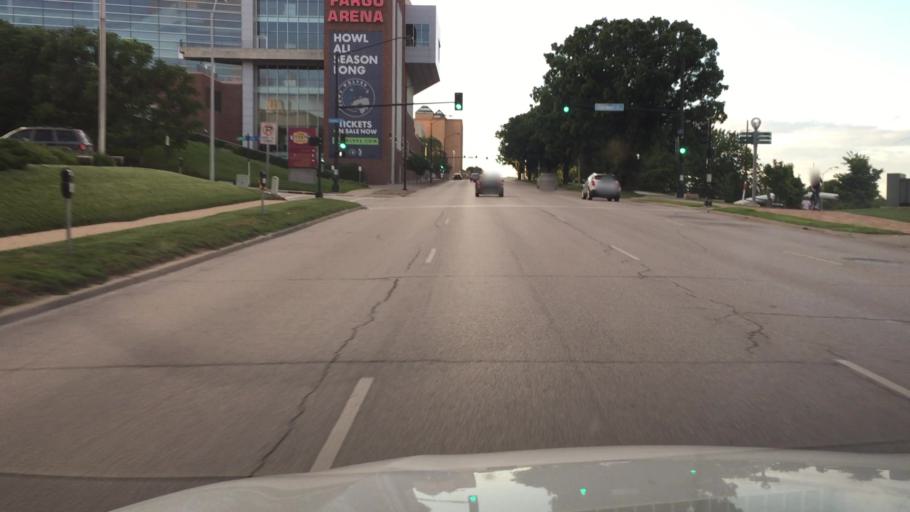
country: US
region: Iowa
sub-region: Polk County
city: Des Moines
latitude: 41.5912
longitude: -93.6204
